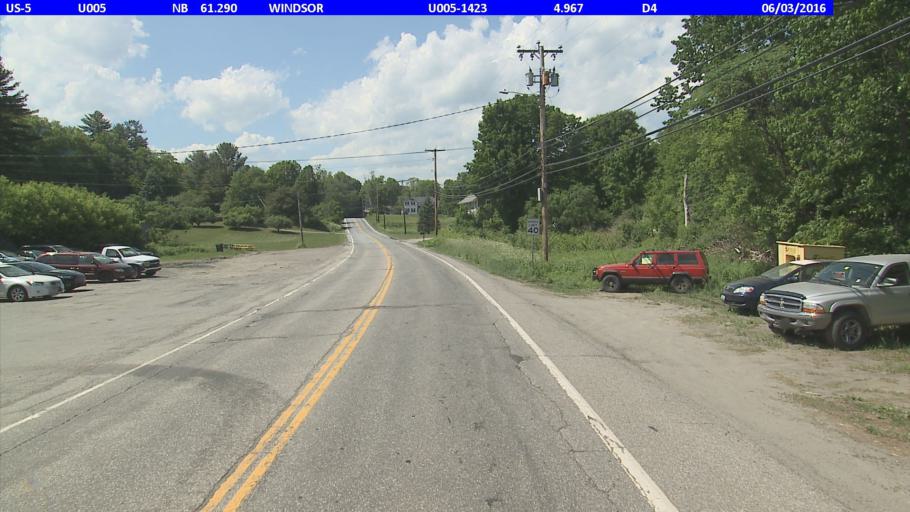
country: US
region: Vermont
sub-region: Windsor County
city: Windsor
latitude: 43.4980
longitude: -72.3892
